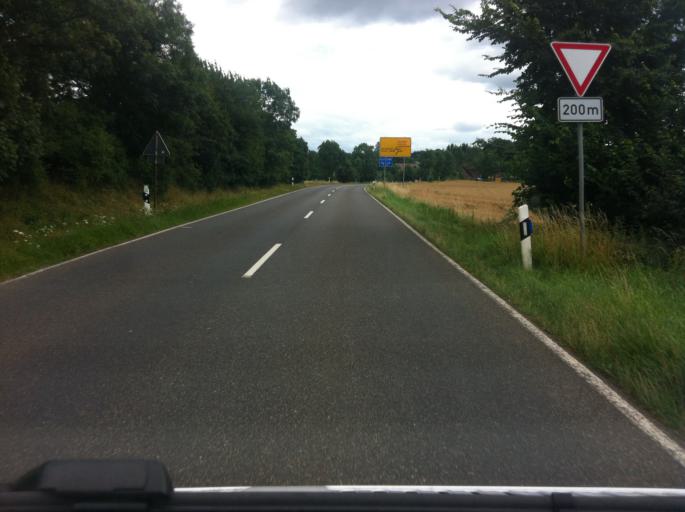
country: DE
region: North Rhine-Westphalia
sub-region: Regierungsbezirk Koln
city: Nettersheim
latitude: 50.5180
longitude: 6.6549
